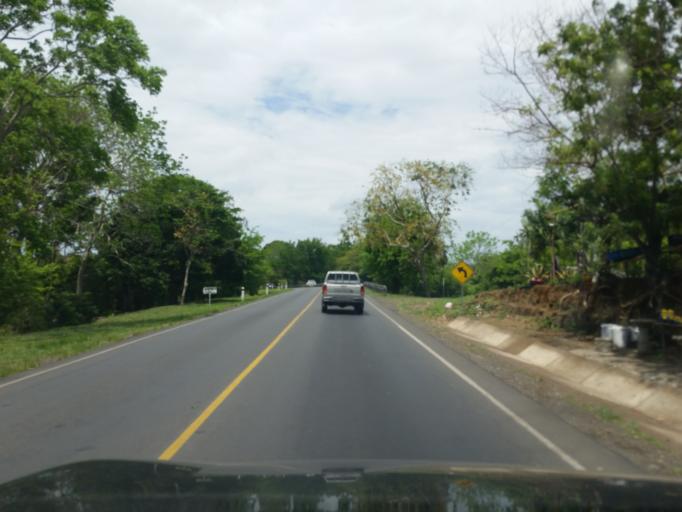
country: NI
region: Masaya
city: Catarina
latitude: 11.9350
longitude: -86.0913
